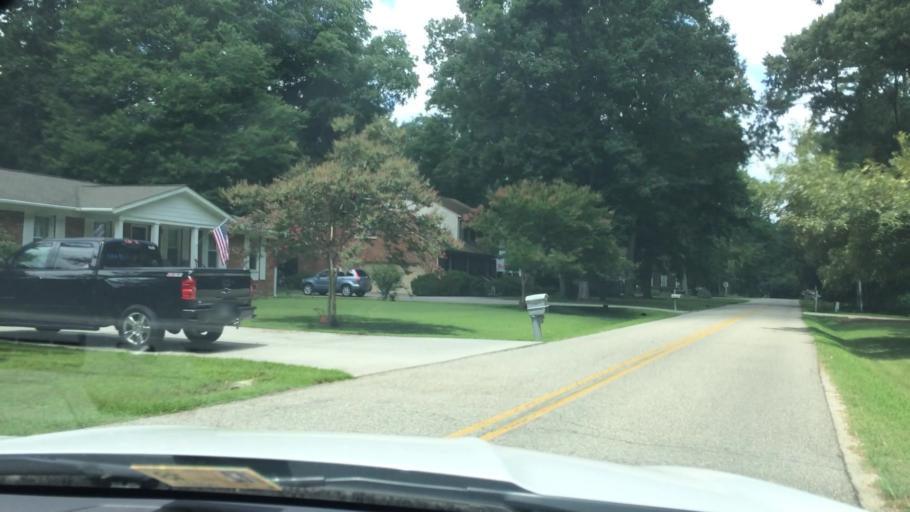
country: US
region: Virginia
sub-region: City of Poquoson
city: Poquoson
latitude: 37.1411
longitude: -76.4410
